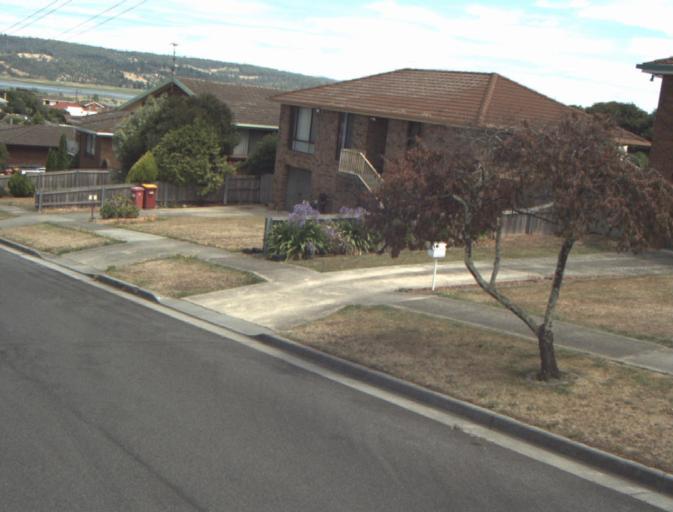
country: AU
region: Tasmania
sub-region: Launceston
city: Mayfield
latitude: -41.3846
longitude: 147.1169
